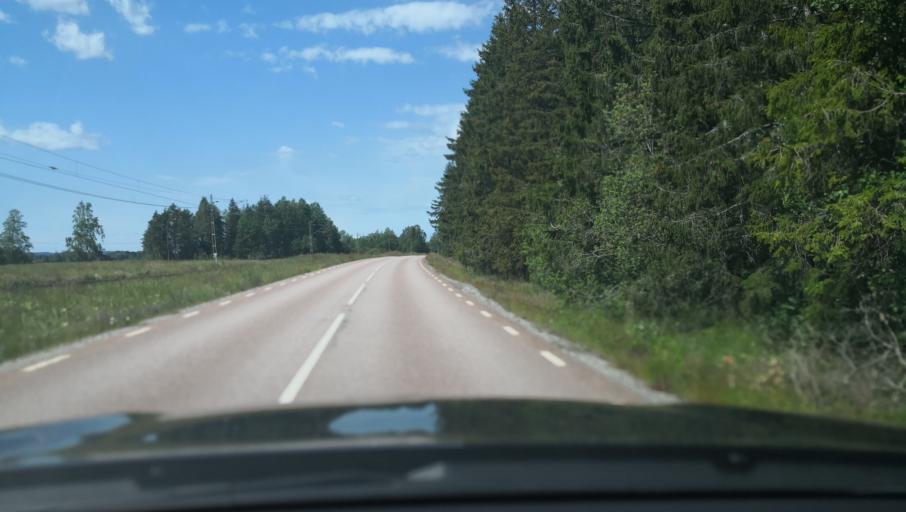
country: SE
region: Vaestmanland
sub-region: Surahammars Kommun
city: Ramnas
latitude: 59.8517
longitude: 16.0979
